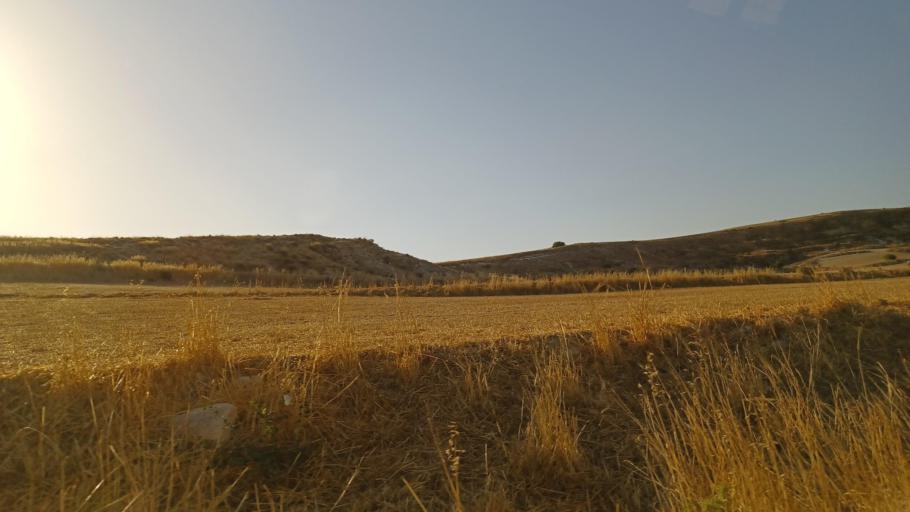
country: CY
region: Larnaka
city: Athienou
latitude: 35.0439
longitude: 33.5211
